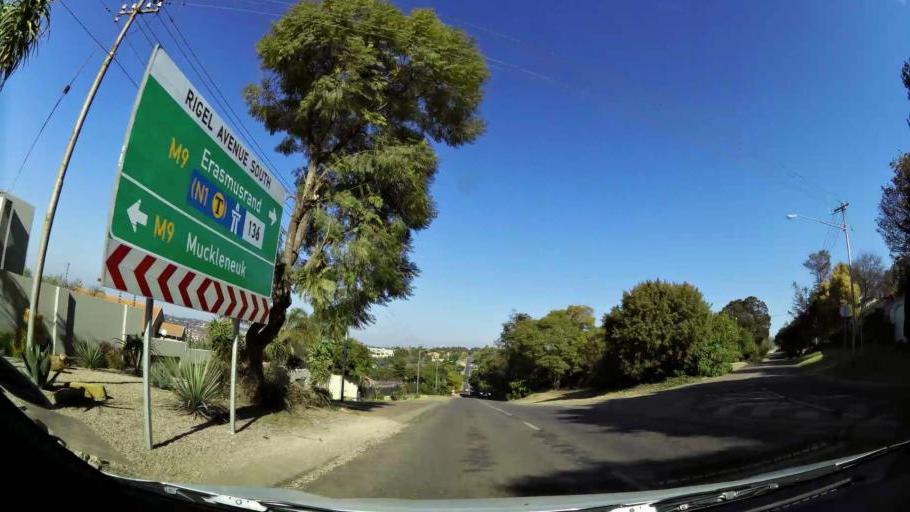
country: ZA
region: Gauteng
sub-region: City of Tshwane Metropolitan Municipality
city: Pretoria
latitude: -25.8009
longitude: 28.2457
